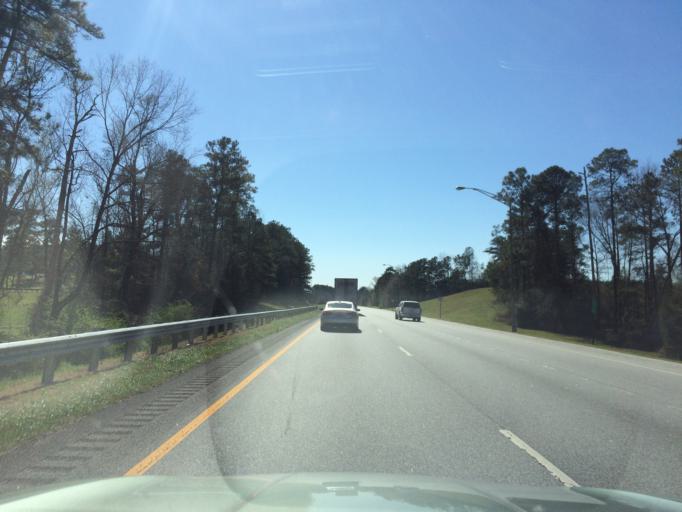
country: US
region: Alabama
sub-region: Macon County
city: Tuskegee
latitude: 32.5016
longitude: -85.6126
